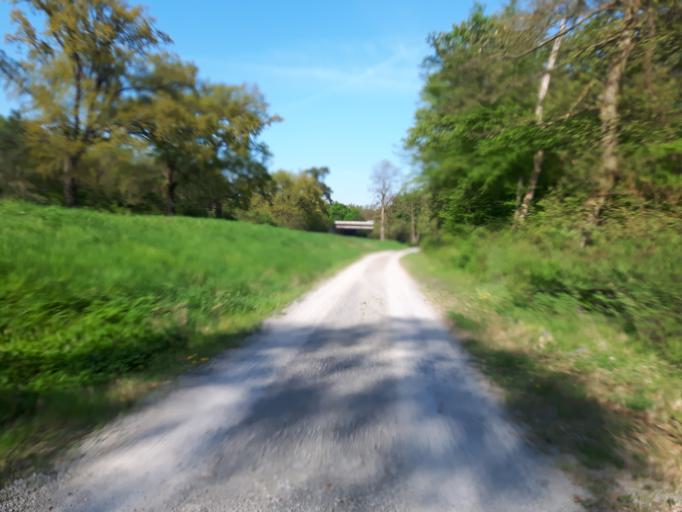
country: DE
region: Baden-Wuerttemberg
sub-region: Karlsruhe Region
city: Hockenheim
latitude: 49.3450
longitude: 8.5516
